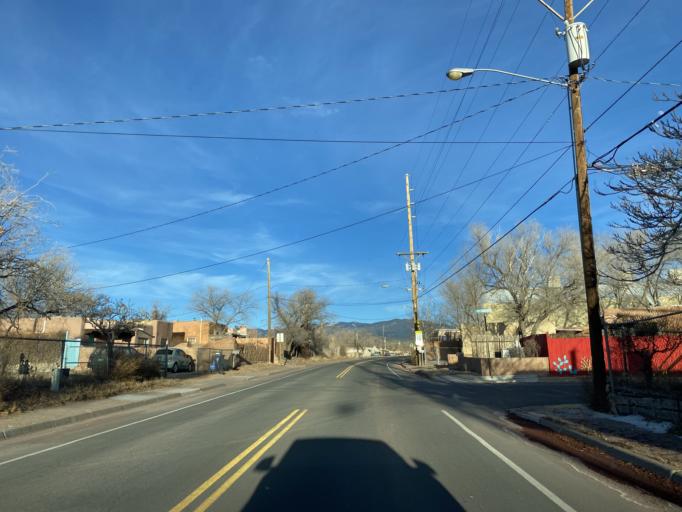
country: US
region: New Mexico
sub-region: Santa Fe County
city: Santa Fe
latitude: 35.6816
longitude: -105.9624
